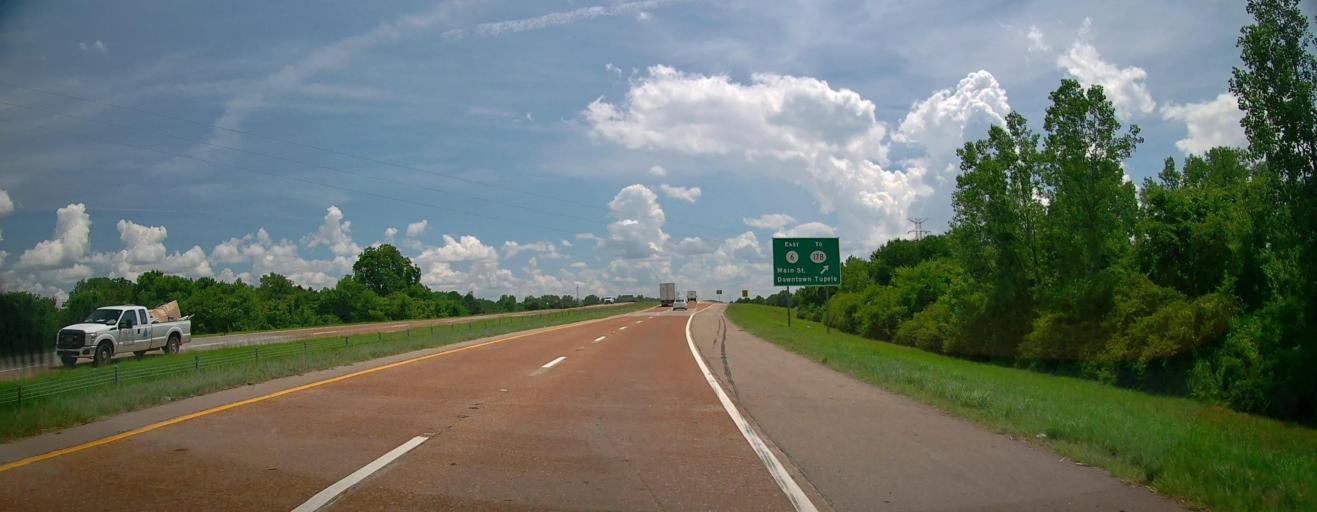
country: US
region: Mississippi
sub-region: Lee County
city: Tupelo
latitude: 34.2646
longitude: -88.6941
